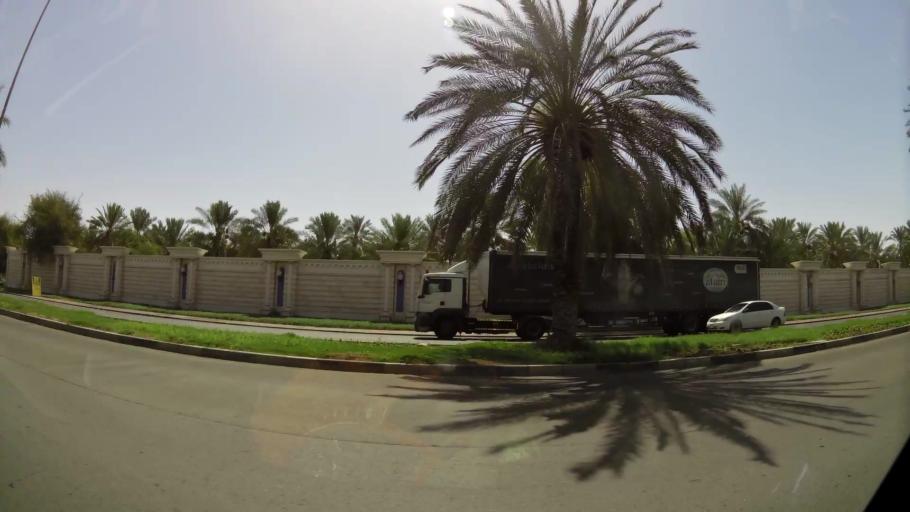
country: OM
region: Al Buraimi
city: Al Buraymi
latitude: 24.2945
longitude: 55.7678
